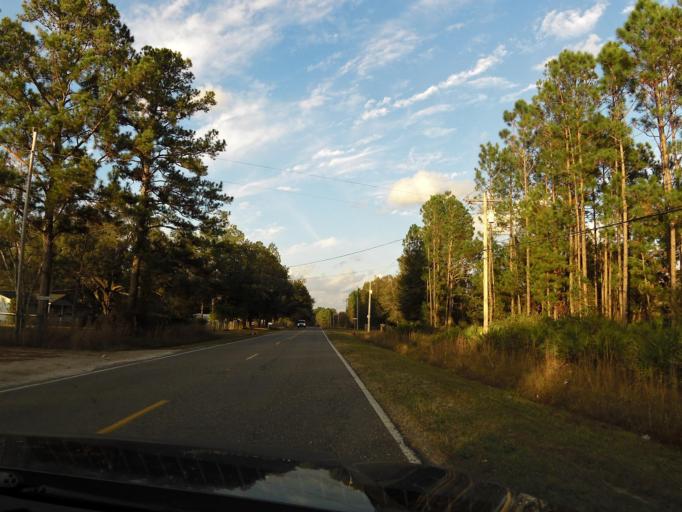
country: US
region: Florida
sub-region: Duval County
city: Baldwin
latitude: 30.1739
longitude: -81.9940
